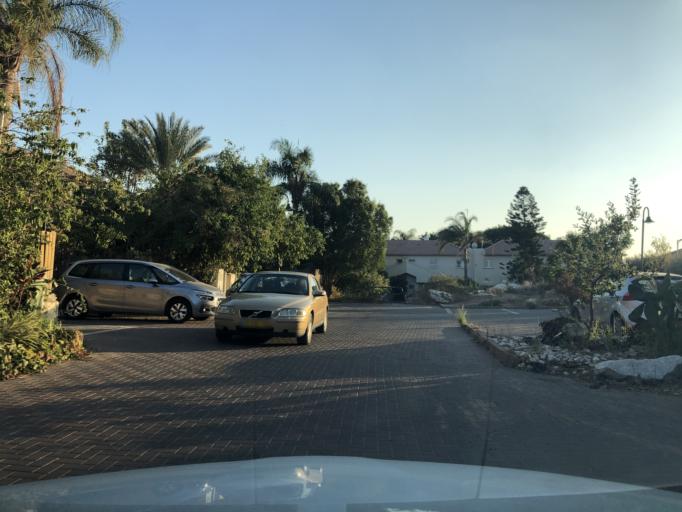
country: PS
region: West Bank
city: Hablah
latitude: 32.1592
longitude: 34.9714
